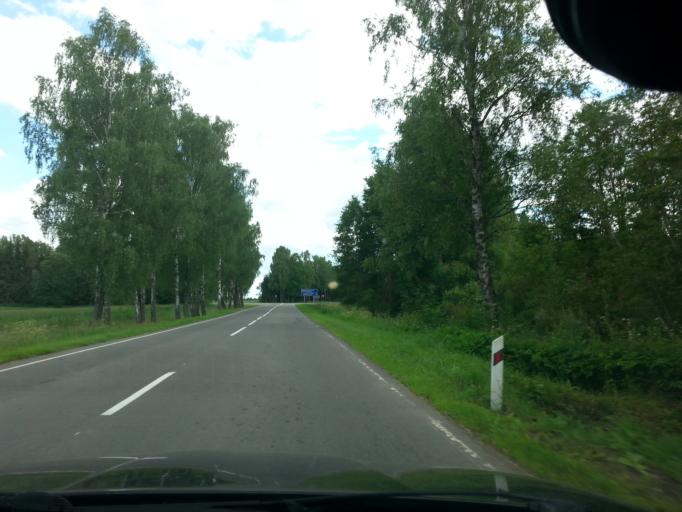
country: BY
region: Minsk
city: Svir
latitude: 54.8935
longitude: 26.3881
